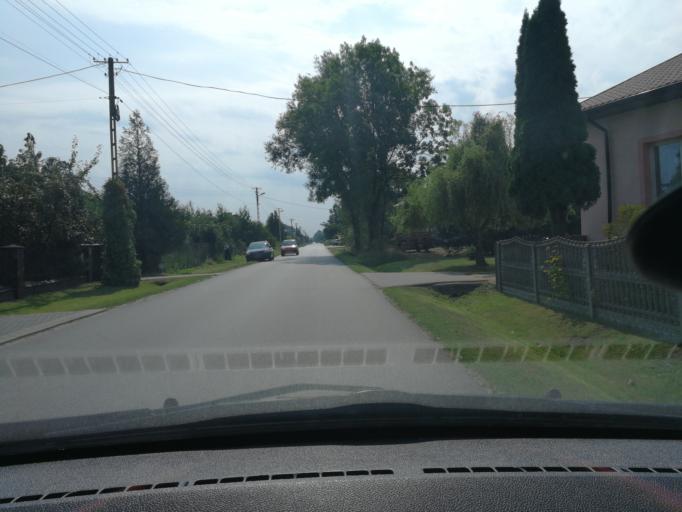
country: PL
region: Lodz Voivodeship
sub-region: Powiat skierniewicki
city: Makow
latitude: 52.0053
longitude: 20.0711
